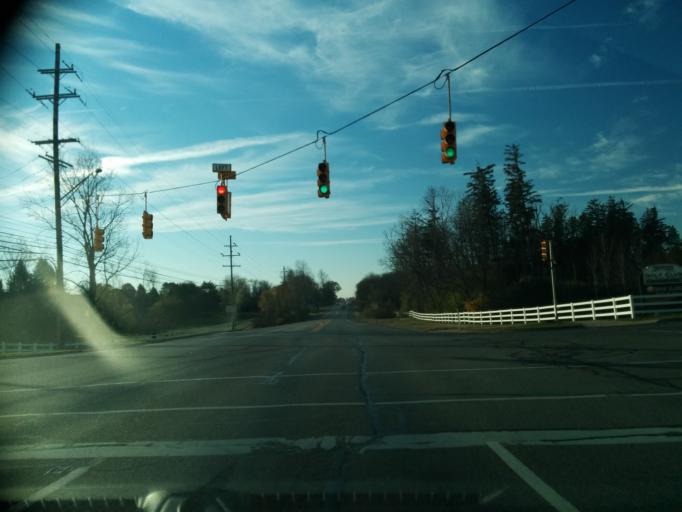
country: US
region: Michigan
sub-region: Oakland County
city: Farmington Hills
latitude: 42.4835
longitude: -83.4166
